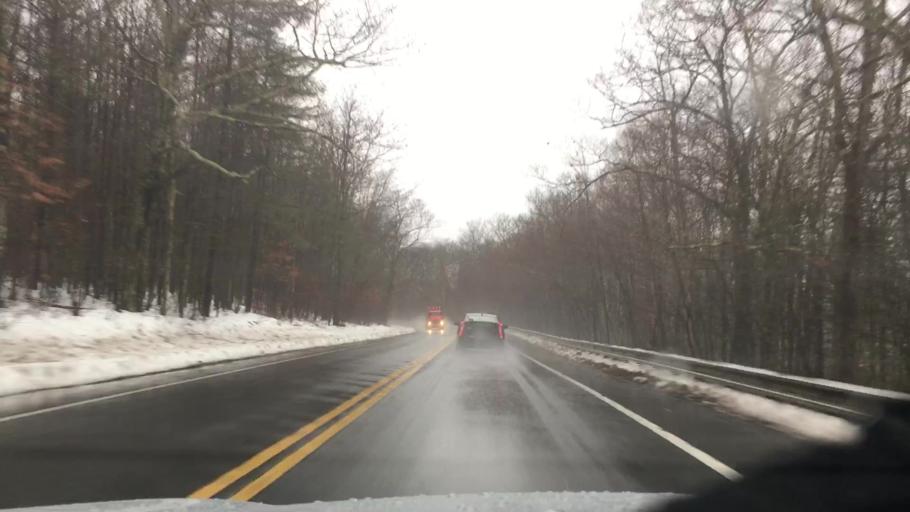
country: US
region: Massachusetts
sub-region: Franklin County
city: Shutesbury
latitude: 42.4414
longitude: -72.3879
